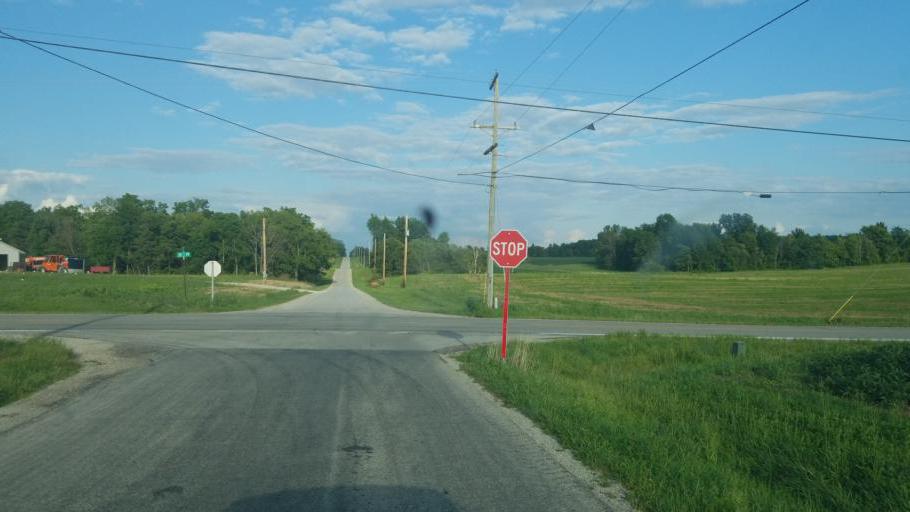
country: US
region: Ohio
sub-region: Sandusky County
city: Green Springs
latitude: 41.1102
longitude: -83.0156
